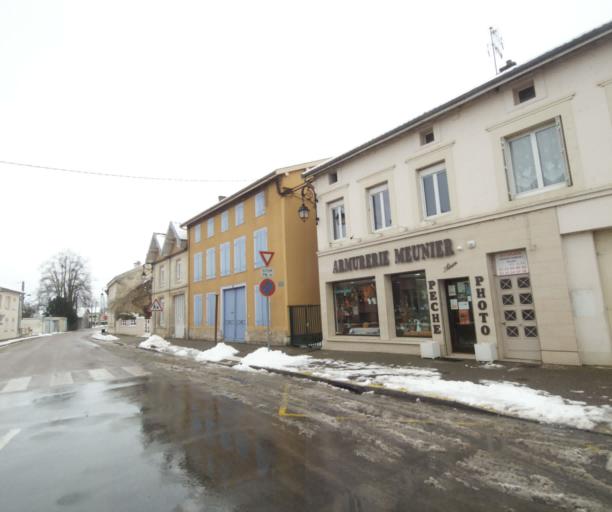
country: FR
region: Champagne-Ardenne
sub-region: Departement de la Haute-Marne
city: Montier-en-Der
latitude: 48.4765
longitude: 4.7716
